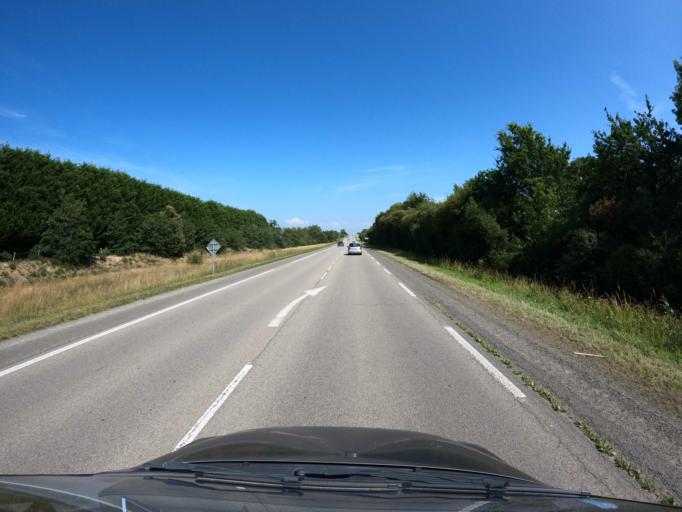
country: FR
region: Pays de la Loire
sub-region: Departement de la Loire-Atlantique
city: Pornic
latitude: 47.1064
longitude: -2.0567
